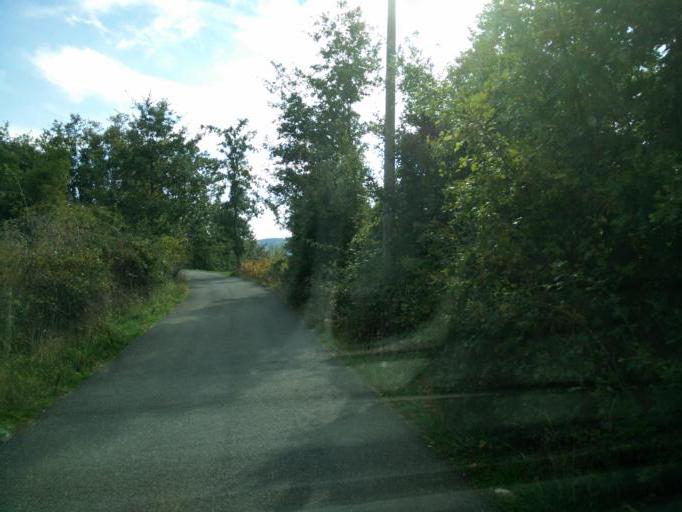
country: IT
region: Tuscany
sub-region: Provincia di Massa-Carrara
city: Patigno
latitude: 44.3553
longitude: 9.7499
